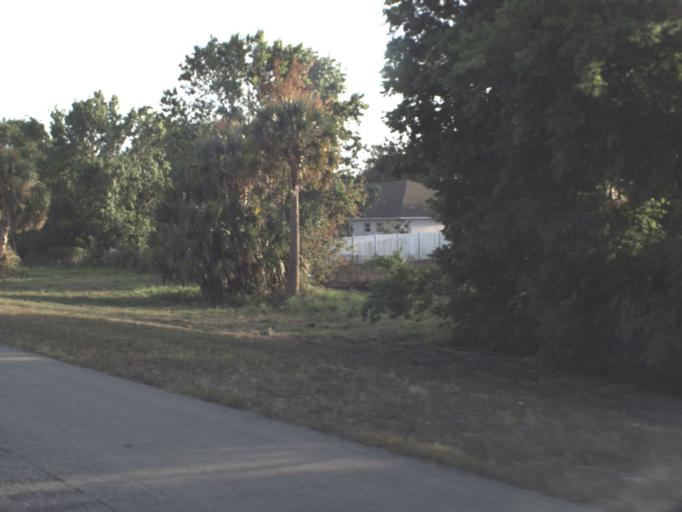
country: US
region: Florida
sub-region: Brevard County
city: Port Saint John
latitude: 28.4621
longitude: -80.8215
